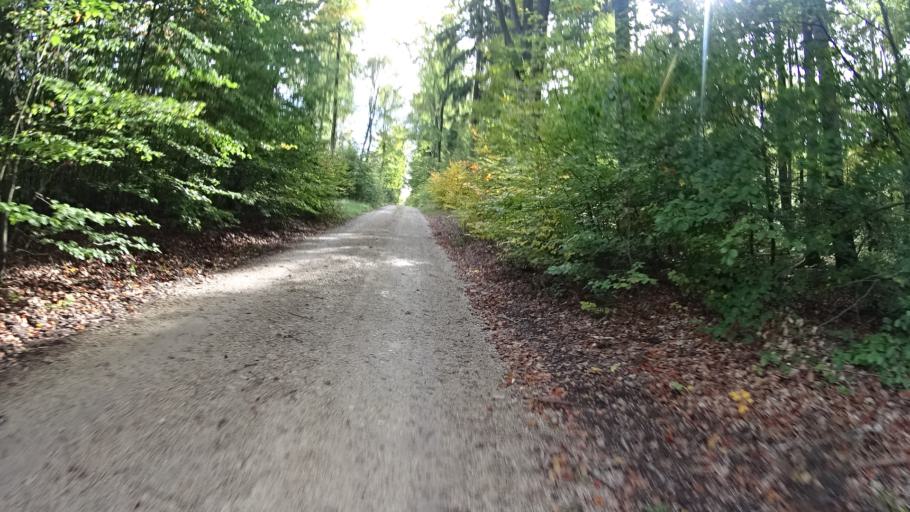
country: DE
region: Bavaria
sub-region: Upper Bavaria
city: Walting
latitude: 48.9086
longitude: 11.3248
